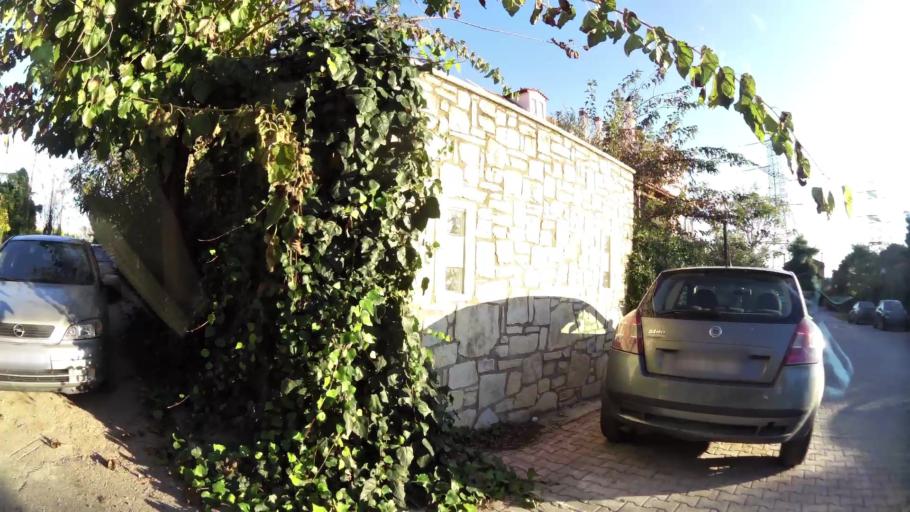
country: GR
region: Attica
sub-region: Nomarchia Anatolikis Attikis
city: Kryoneri
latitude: 38.1356
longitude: 23.8307
